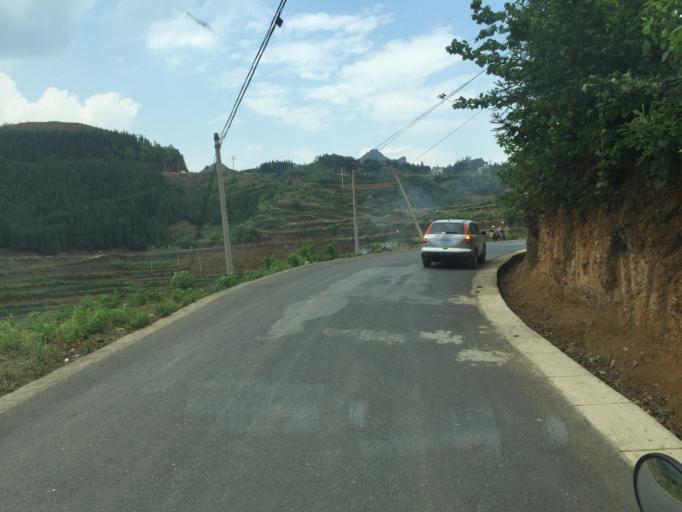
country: CN
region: Guangxi Zhuangzu Zizhiqu
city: Xinzhou
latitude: 25.6546
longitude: 105.2364
